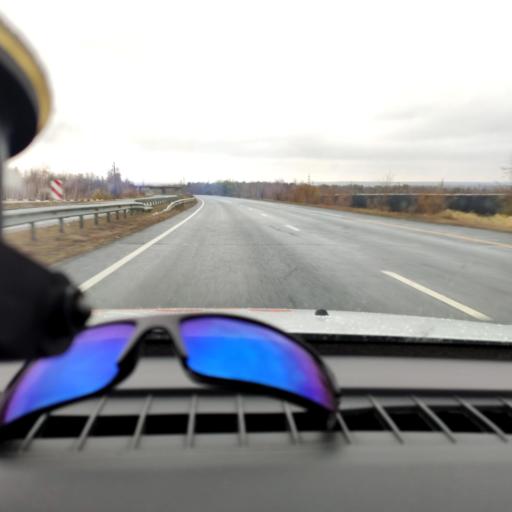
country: RU
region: Samara
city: Novokuybyshevsk
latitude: 53.0156
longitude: 49.9810
